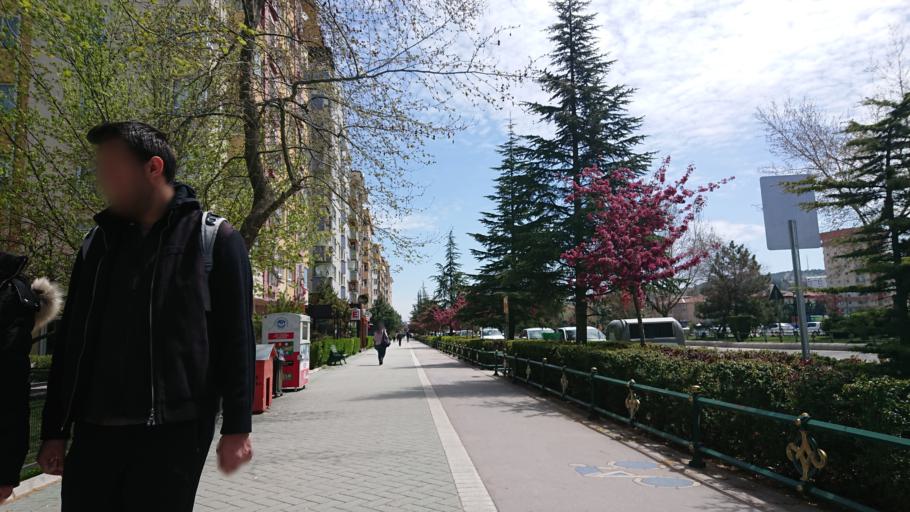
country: TR
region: Eskisehir
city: Eskisehir
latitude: 39.7651
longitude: 30.5054
